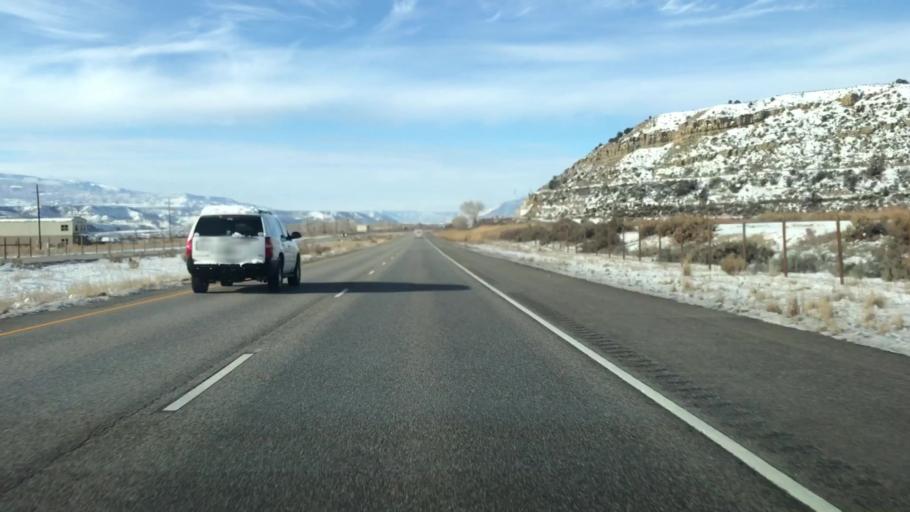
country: US
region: Colorado
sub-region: Garfield County
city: Silt
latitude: 39.5471
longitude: -107.6202
